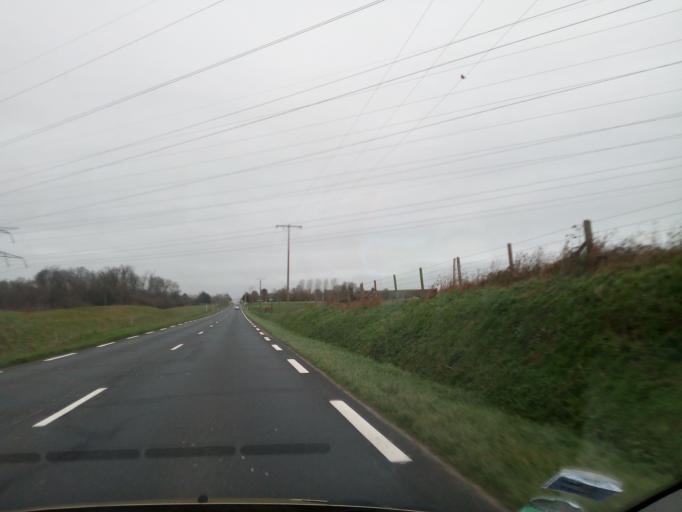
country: FR
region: Haute-Normandie
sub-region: Departement de l'Eure
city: Bourg-Achard
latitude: 49.3781
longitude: 0.8050
